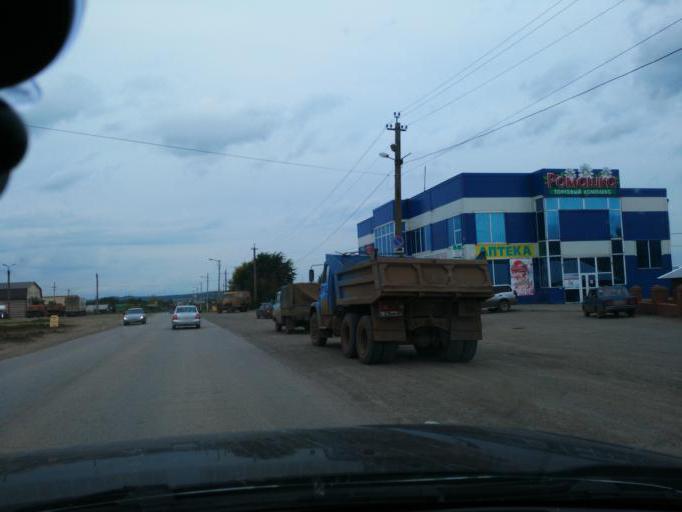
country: RU
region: Perm
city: Chernushka
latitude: 56.5339
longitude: 56.0967
